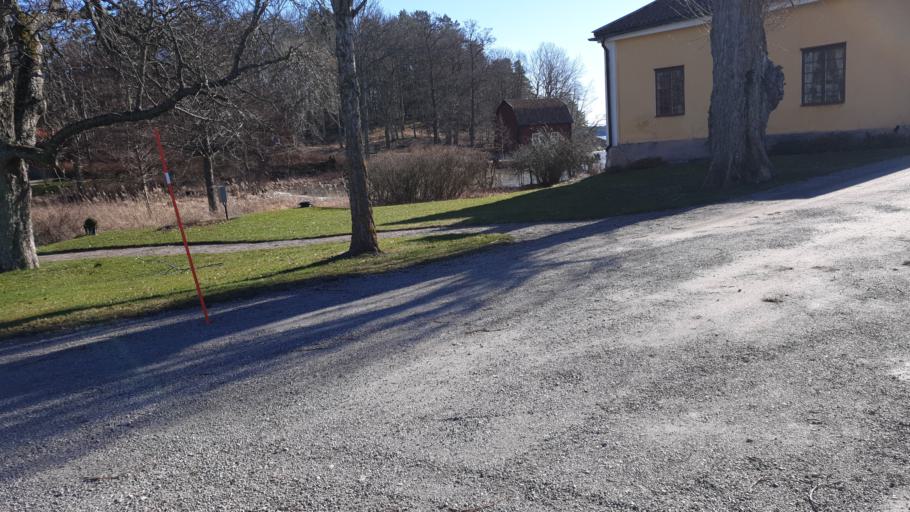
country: SE
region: Soedermanland
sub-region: Strangnas Kommun
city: Stallarholmen
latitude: 59.4726
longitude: 17.2470
